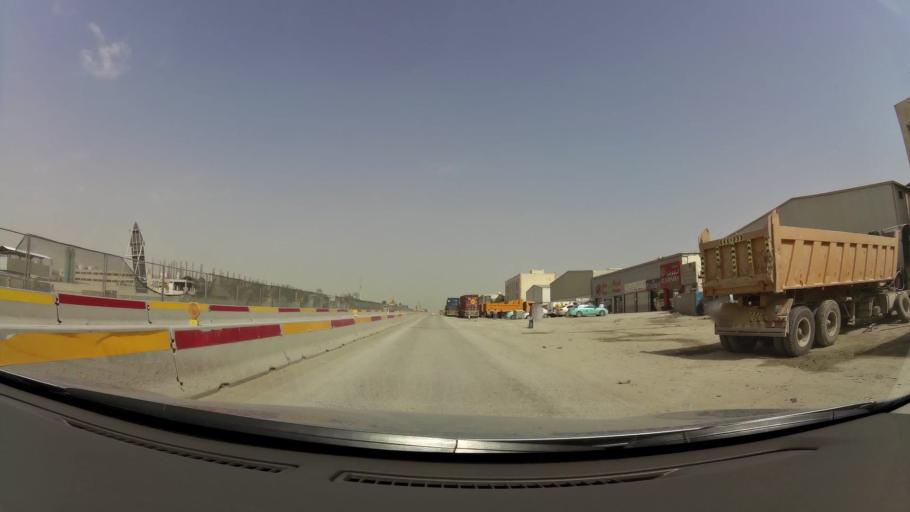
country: QA
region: Al Wakrah
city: Al Wukayr
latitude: 25.1658
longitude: 51.4531
